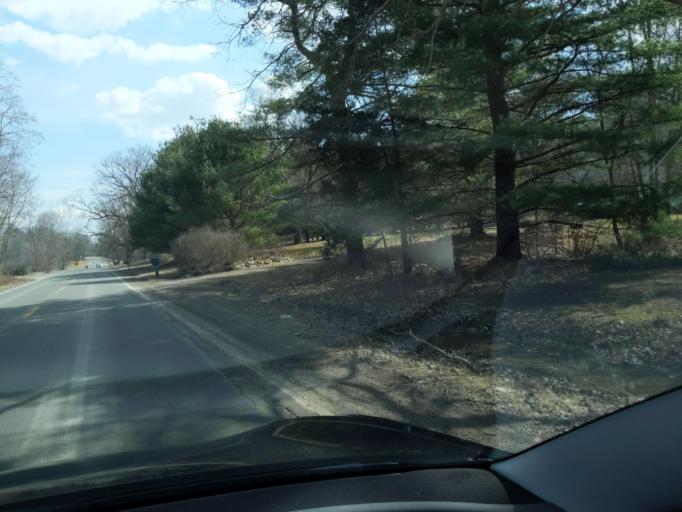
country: US
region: Michigan
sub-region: Washtenaw County
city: Dexter
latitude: 42.3851
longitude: -83.8995
